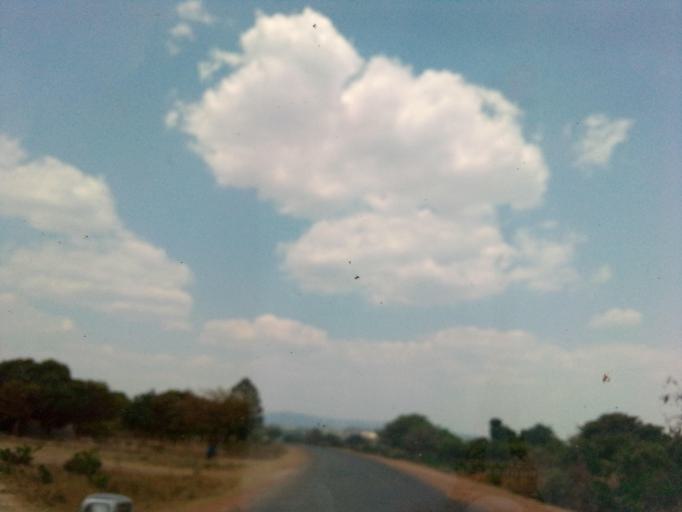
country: ZM
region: Northern
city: Mpika
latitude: -11.8360
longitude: 31.3846
